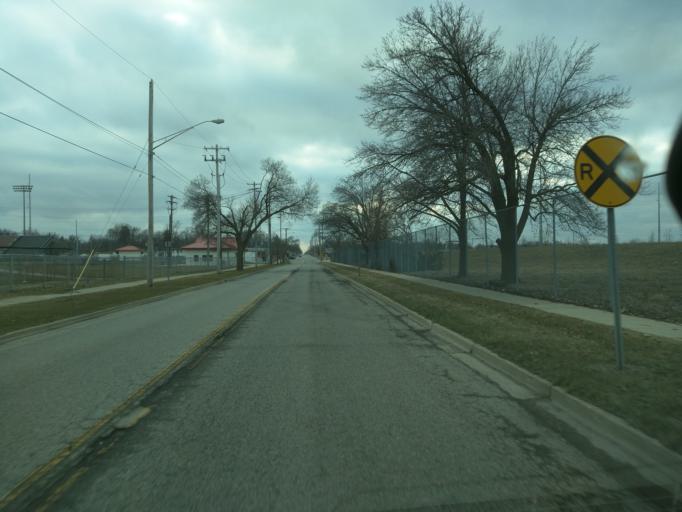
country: US
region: Michigan
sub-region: Ingham County
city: Edgemont Park
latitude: 42.7338
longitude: -84.5791
